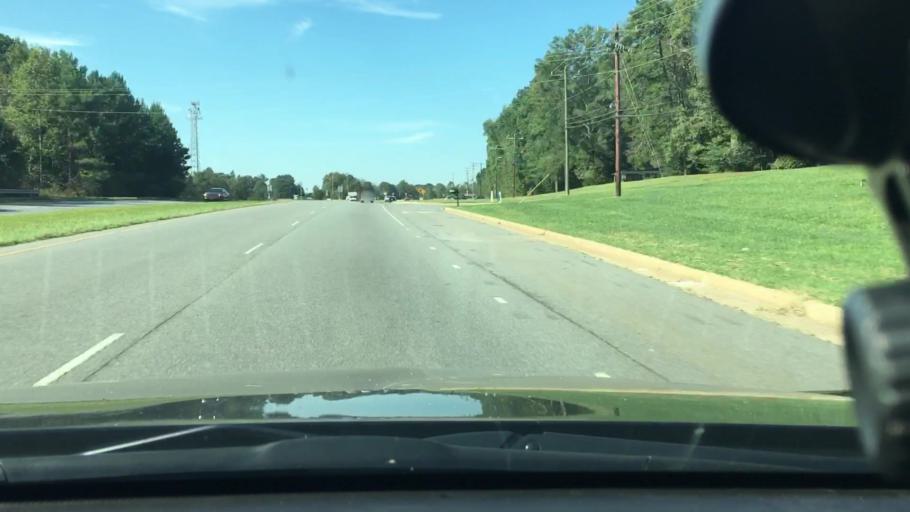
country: US
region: North Carolina
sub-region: Mecklenburg County
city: Mint Hill
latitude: 35.2277
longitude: -80.6105
